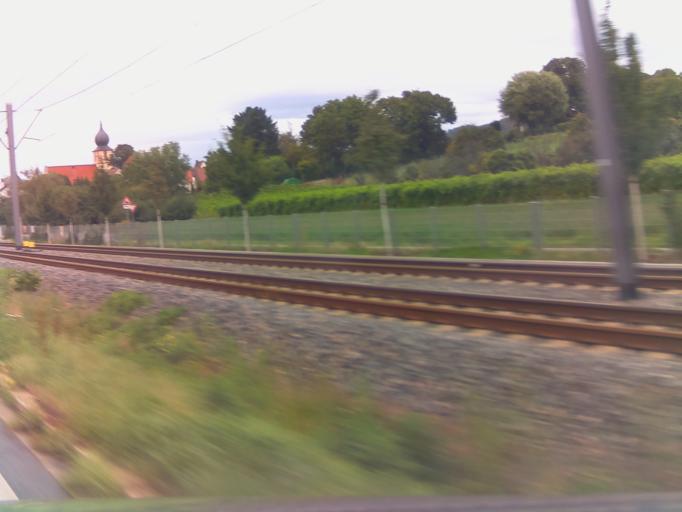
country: DE
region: Baden-Wuerttemberg
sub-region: Karlsruhe Region
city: Schriesheim
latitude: 49.5075
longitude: 8.6560
